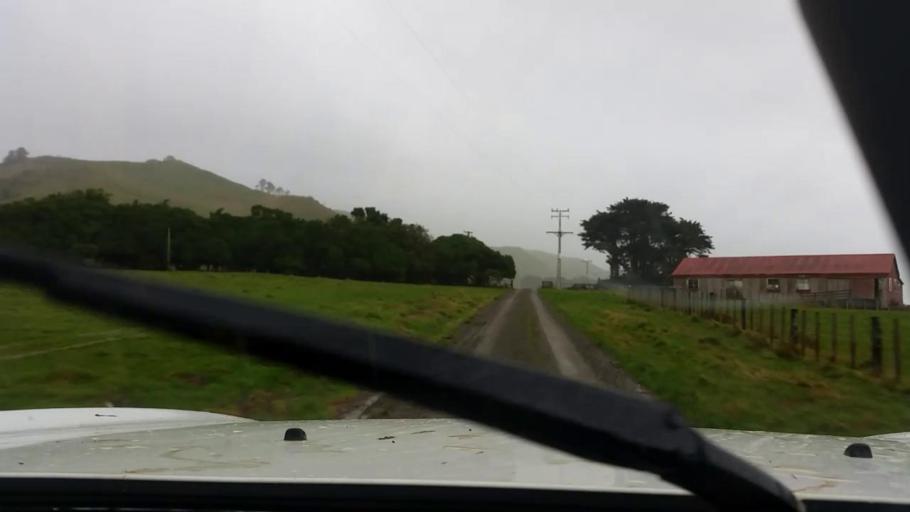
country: NZ
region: Wellington
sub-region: Masterton District
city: Masterton
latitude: -41.2628
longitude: 175.8943
